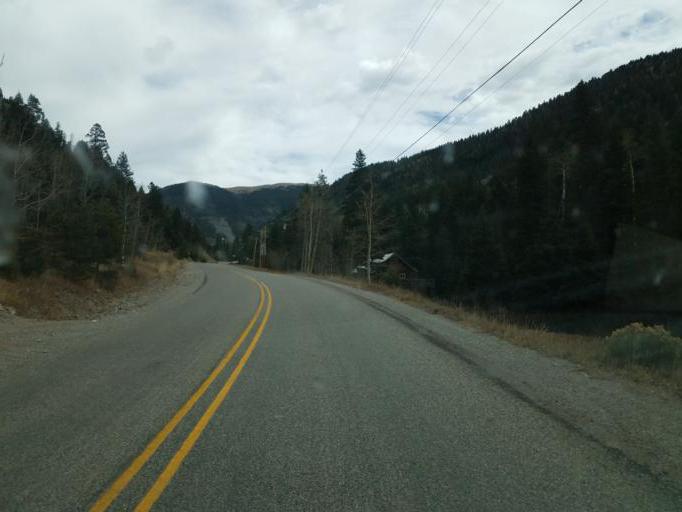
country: US
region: New Mexico
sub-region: Taos County
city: Arroyo Seco
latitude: 36.5954
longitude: -105.4729
